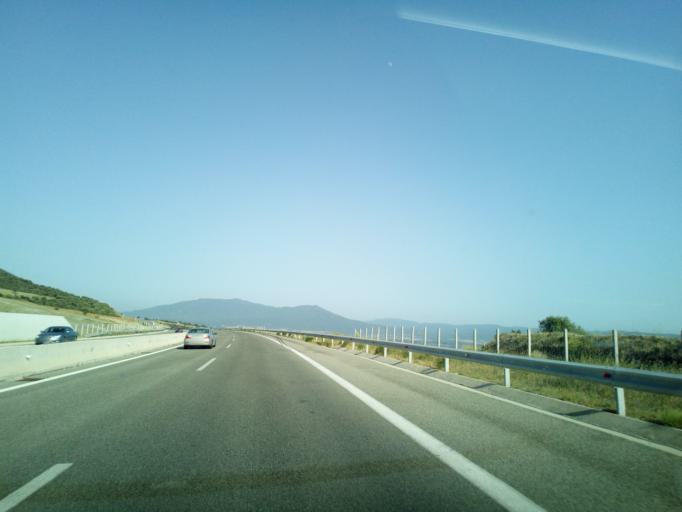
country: GR
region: Central Macedonia
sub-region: Nomos Thessalonikis
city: Nea Apollonia
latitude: 40.6878
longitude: 23.5364
